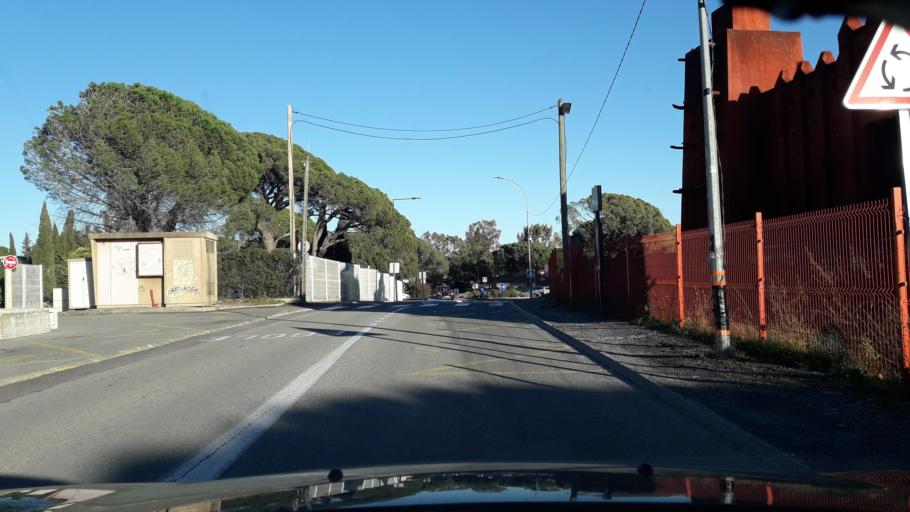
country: FR
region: Provence-Alpes-Cote d'Azur
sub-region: Departement du Var
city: Frejus
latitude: 43.4578
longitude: 6.7269
